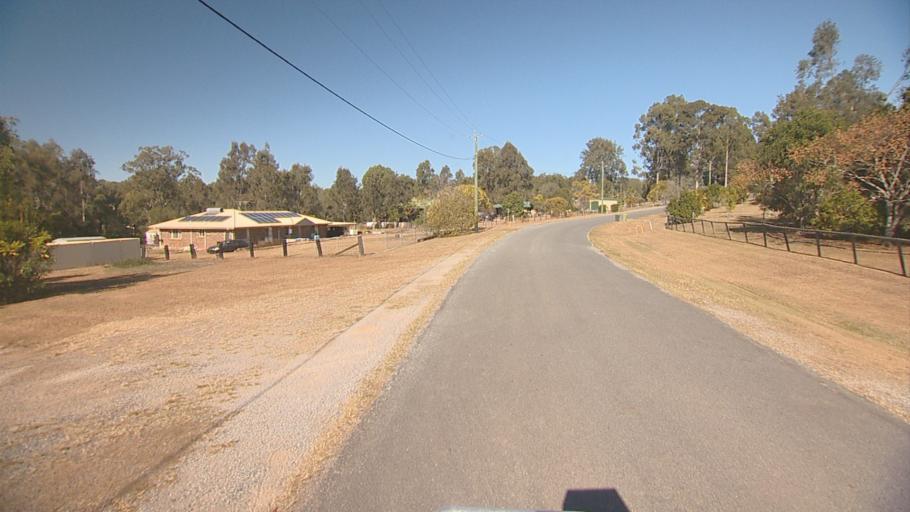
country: AU
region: Queensland
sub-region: Logan
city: Cedar Vale
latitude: -27.8697
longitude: 153.0068
